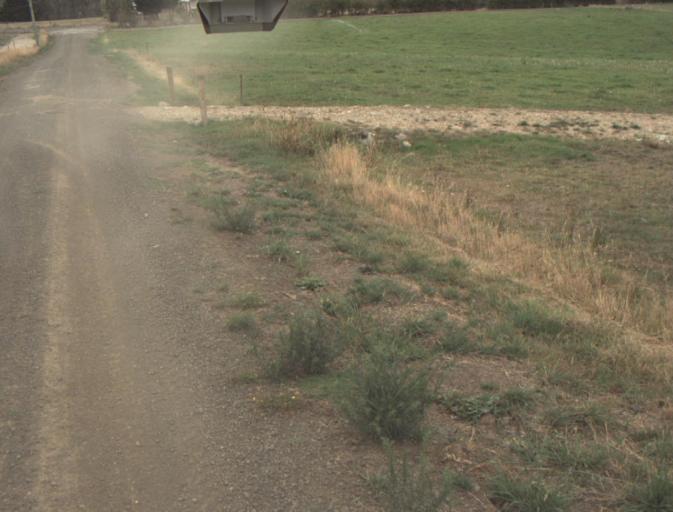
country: AU
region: Tasmania
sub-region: Launceston
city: Mayfield
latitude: -41.2388
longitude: 147.2064
